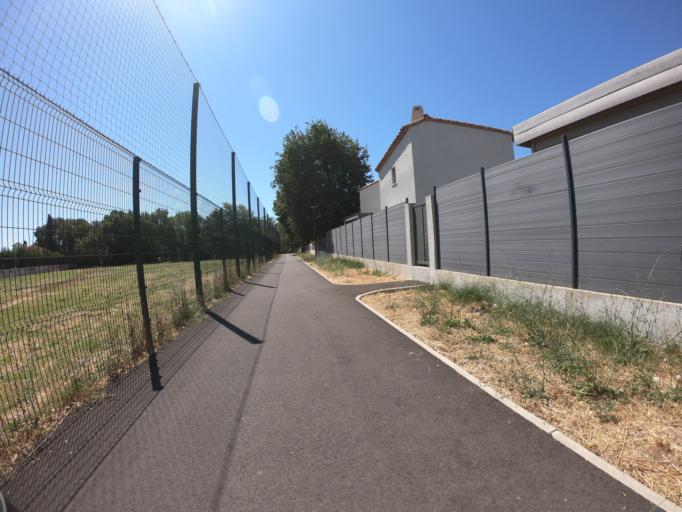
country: FR
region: Provence-Alpes-Cote d'Azur
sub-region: Departement du Var
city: La Garde
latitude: 43.1318
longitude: 6.0215
